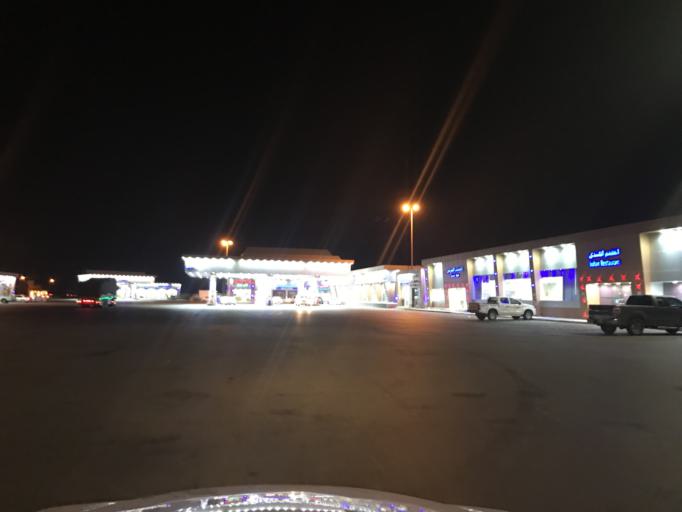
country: SA
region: Ar Riyad
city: Tumayr
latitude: 25.5271
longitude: 45.9459
